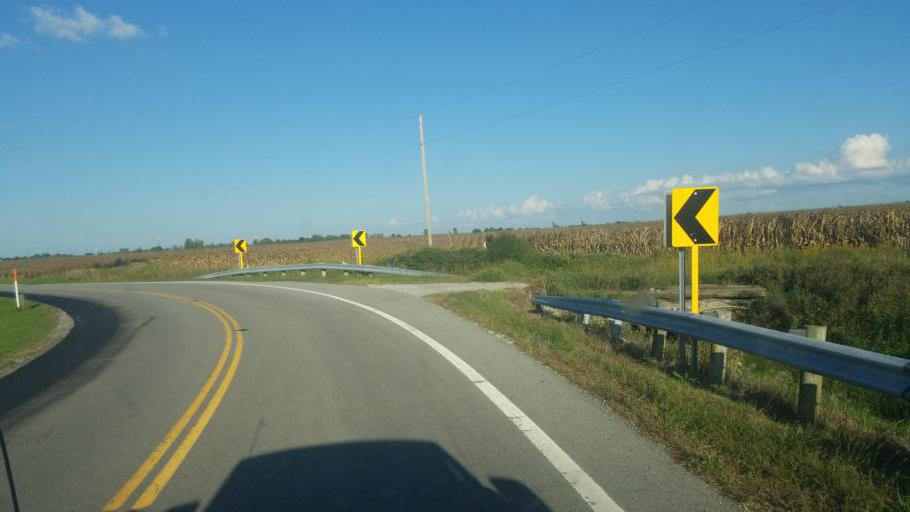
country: US
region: Ohio
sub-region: Wyandot County
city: Carey
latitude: 40.9343
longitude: -83.4157
